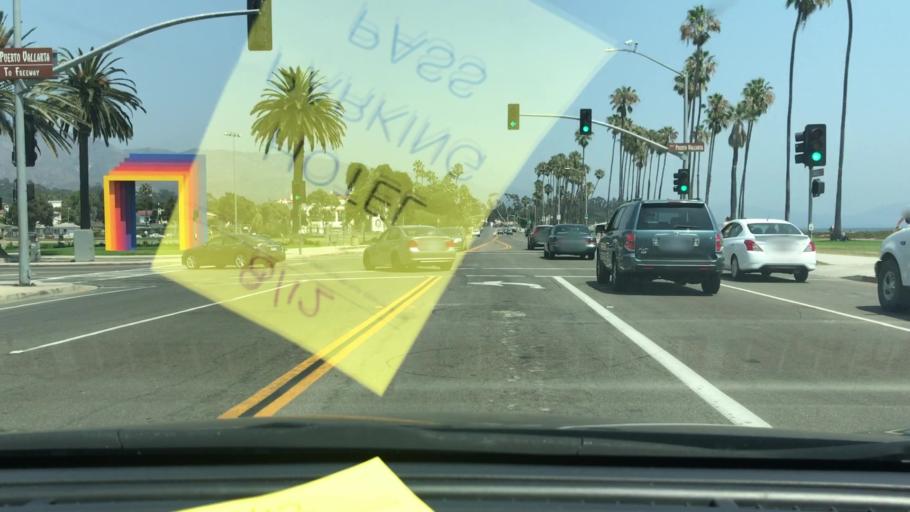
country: US
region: California
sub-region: Santa Barbara County
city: Santa Barbara
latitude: 34.4161
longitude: -119.6756
